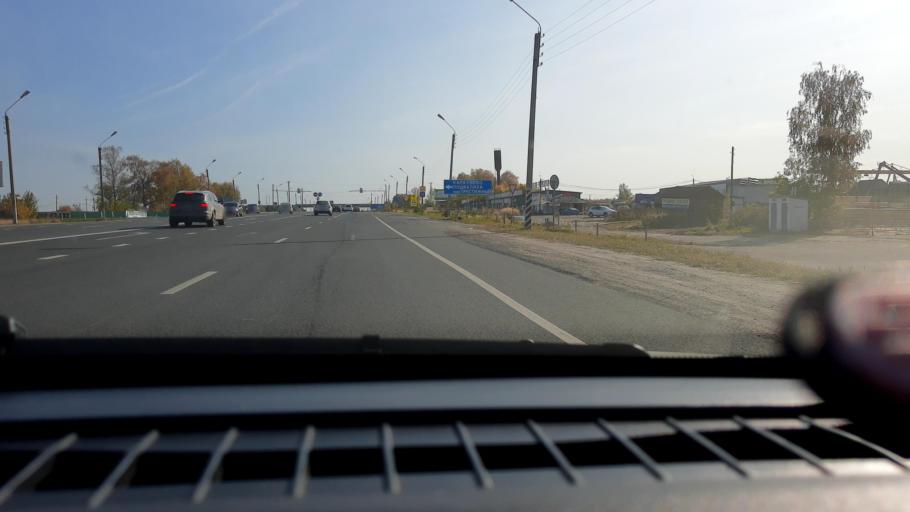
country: RU
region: Nizjnij Novgorod
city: Kstovo
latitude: 56.1305
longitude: 44.2532
